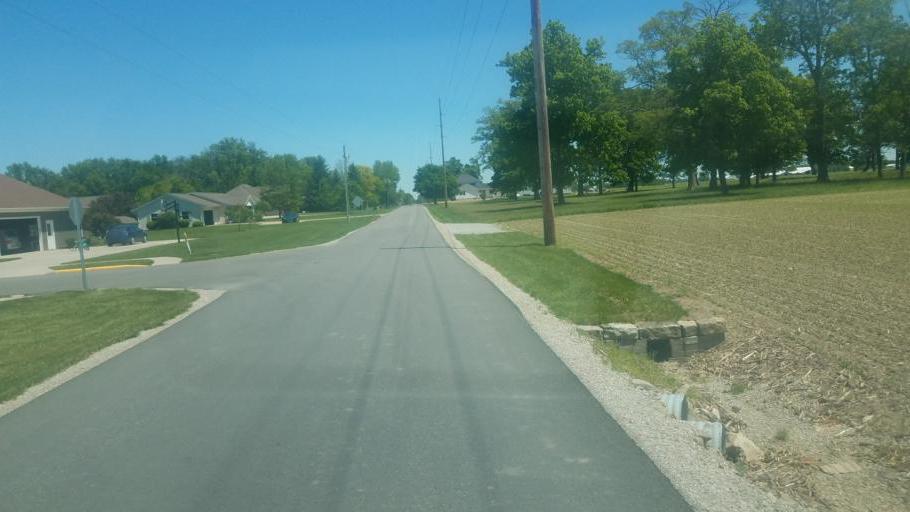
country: US
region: Ohio
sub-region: Darke County
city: Versailles
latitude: 40.2264
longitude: -84.4124
